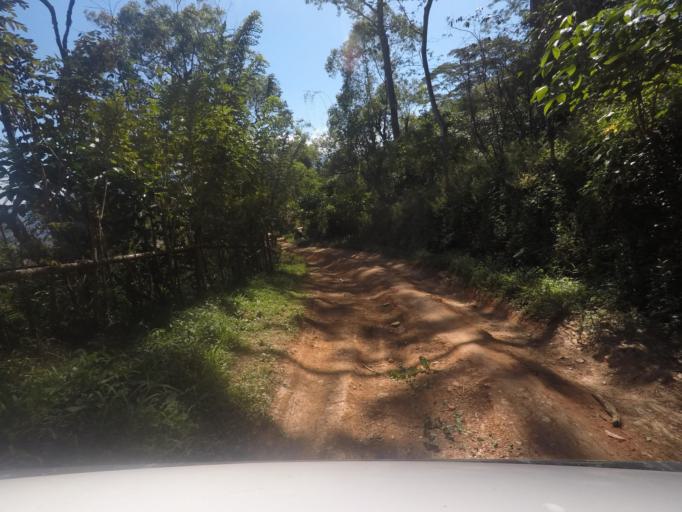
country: TL
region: Ermera
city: Gleno
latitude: -8.7203
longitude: 125.3224
